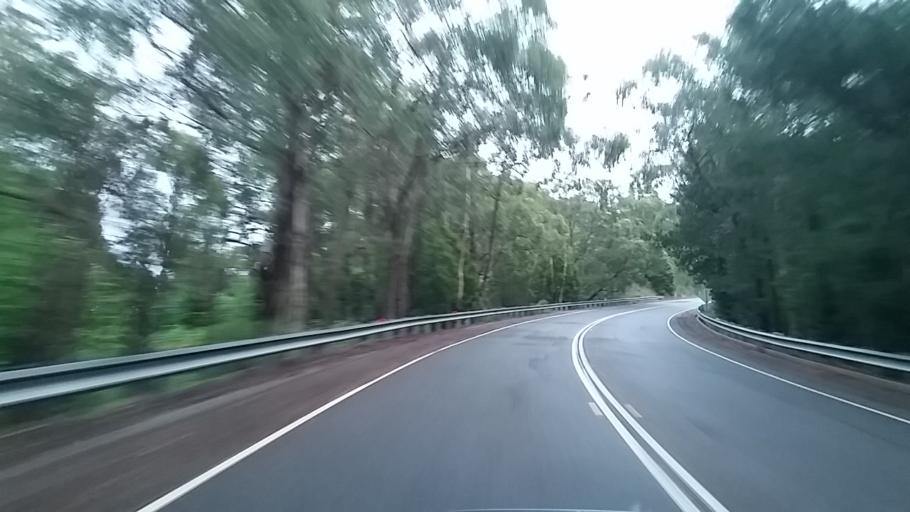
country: AU
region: South Australia
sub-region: Adelaide Hills
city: Crafers
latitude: -34.9912
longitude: 138.7086
